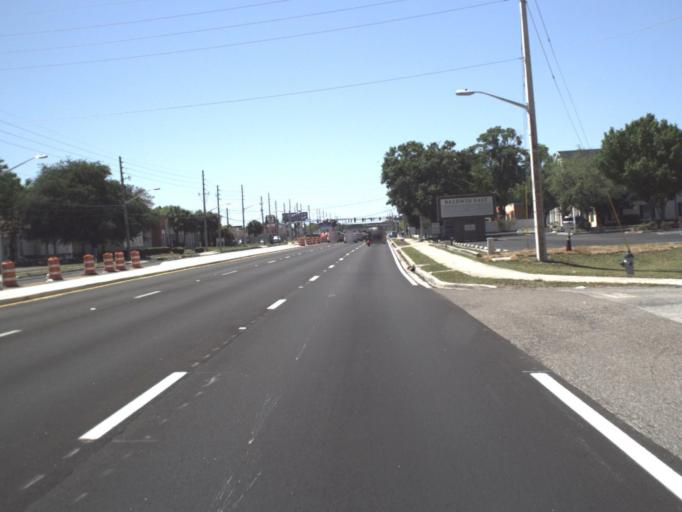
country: US
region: Florida
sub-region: Orange County
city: Union Park
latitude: 28.5649
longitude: -81.3110
